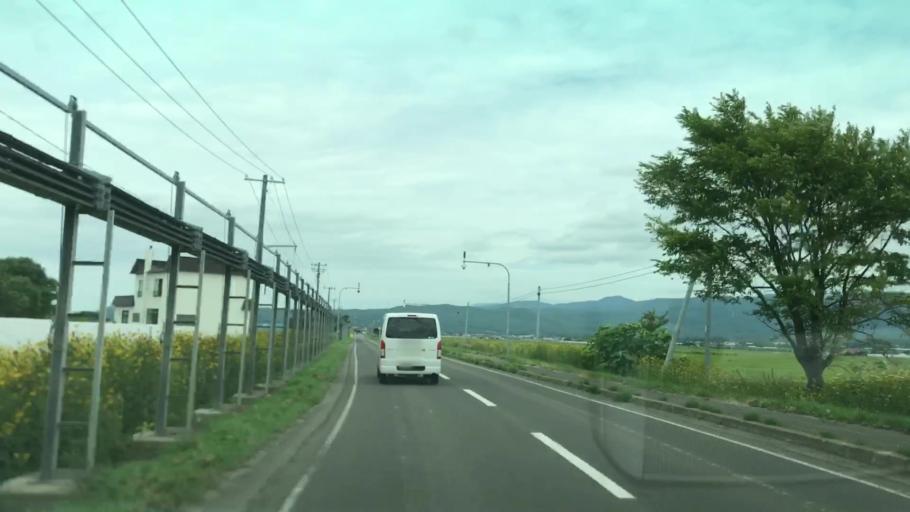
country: JP
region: Hokkaido
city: Iwanai
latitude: 43.0044
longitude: 140.5841
